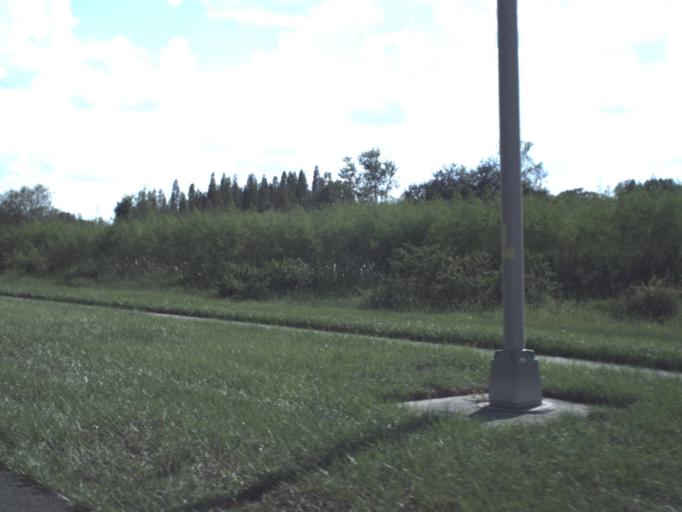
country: US
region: Florida
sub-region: Polk County
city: Fuller Heights
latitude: 27.9324
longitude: -81.9742
